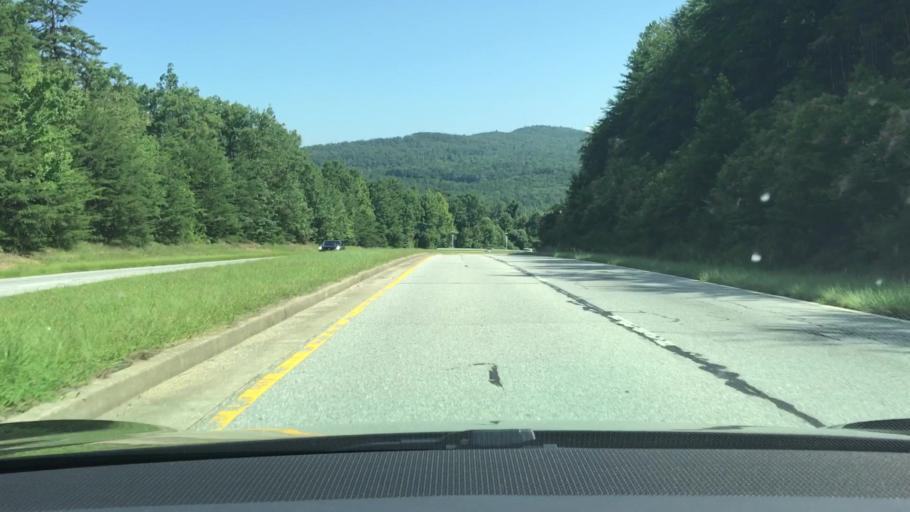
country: US
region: Georgia
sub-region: Rabun County
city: Clayton
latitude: 34.7286
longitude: -83.3906
